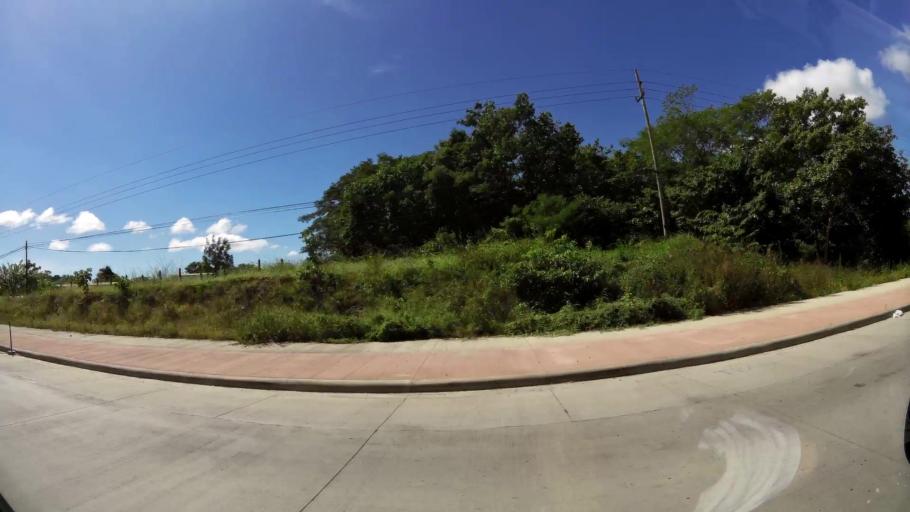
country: CR
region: Guanacaste
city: Bagaces
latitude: 10.5125
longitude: -85.2372
